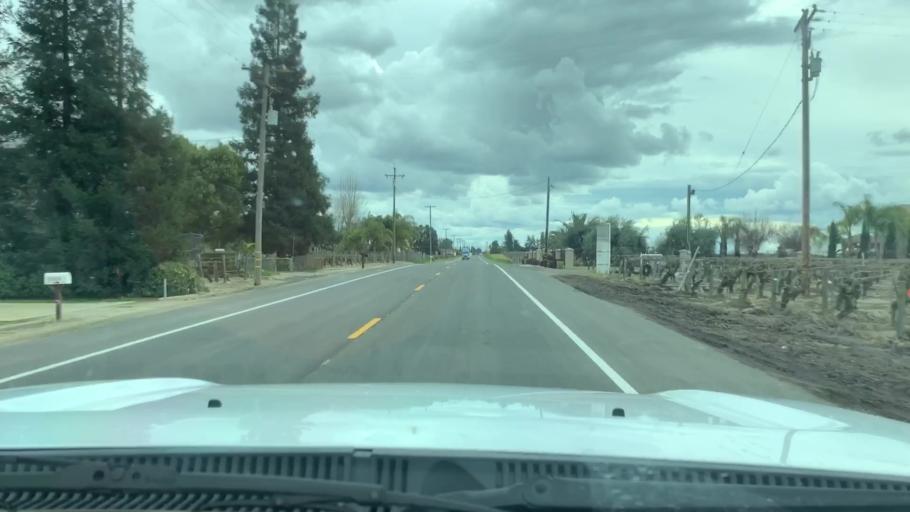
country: US
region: California
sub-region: Fresno County
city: Fowler
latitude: 36.5667
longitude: -119.6825
